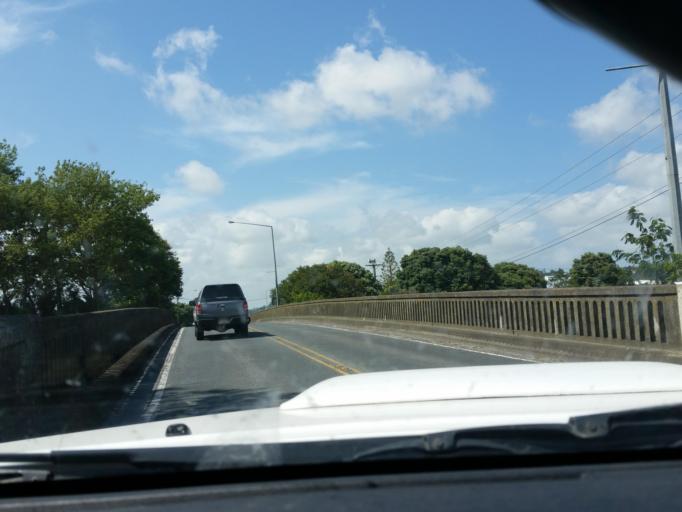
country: NZ
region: Northland
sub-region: Kaipara District
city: Dargaville
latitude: -35.9443
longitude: 173.8662
